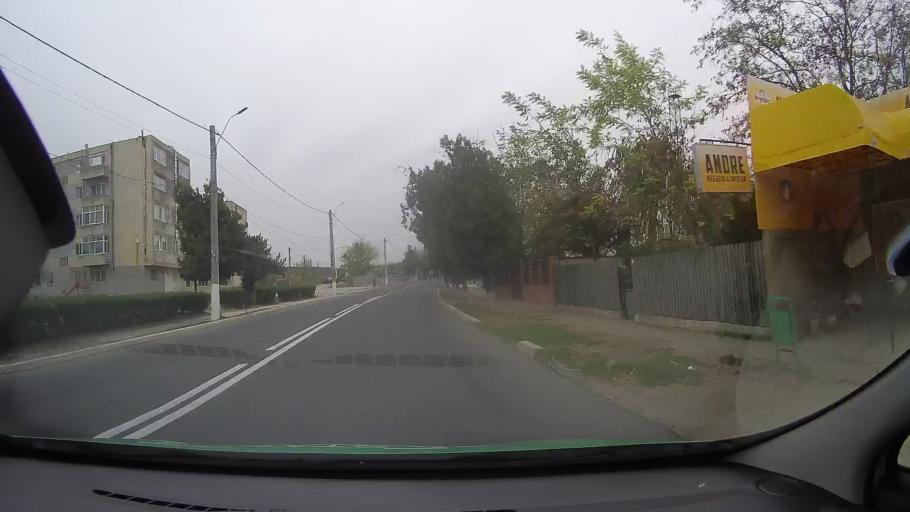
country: RO
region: Constanta
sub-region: Oras Harsova
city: Harsova
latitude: 44.6898
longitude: 27.9429
